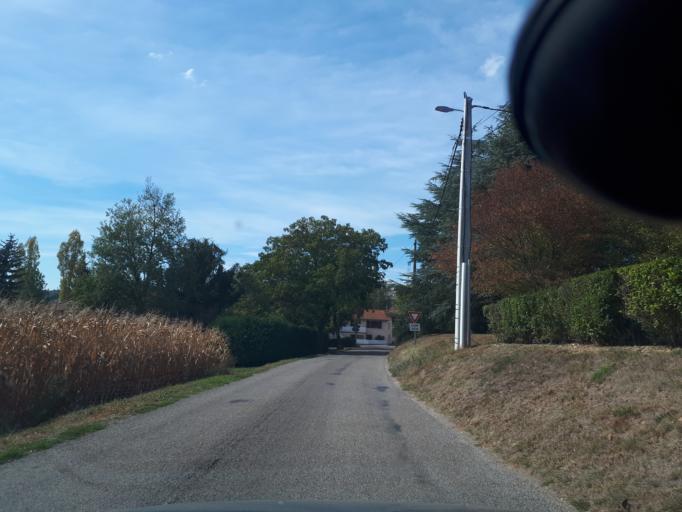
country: FR
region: Rhone-Alpes
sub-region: Departement de l'Isere
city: Chatonnay
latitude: 45.5107
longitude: 5.2050
